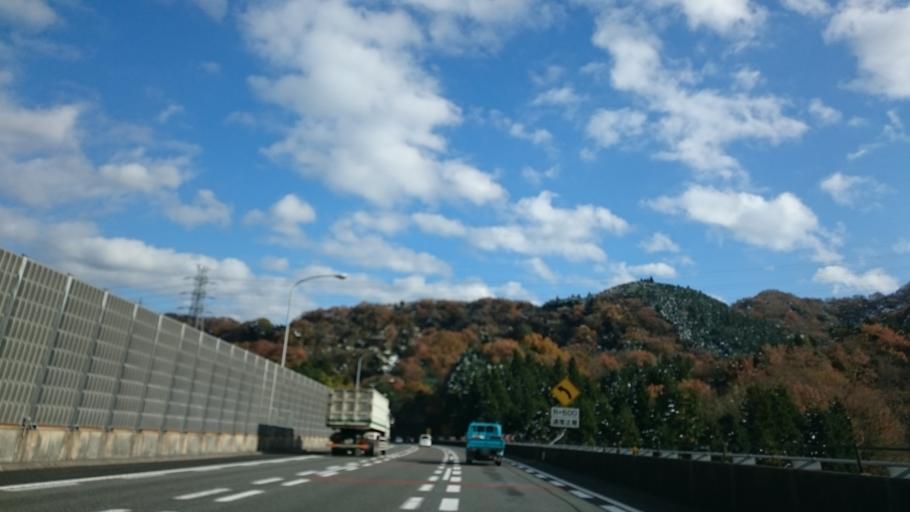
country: JP
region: Shizuoka
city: Gotemba
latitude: 35.3502
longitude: 139.0029
